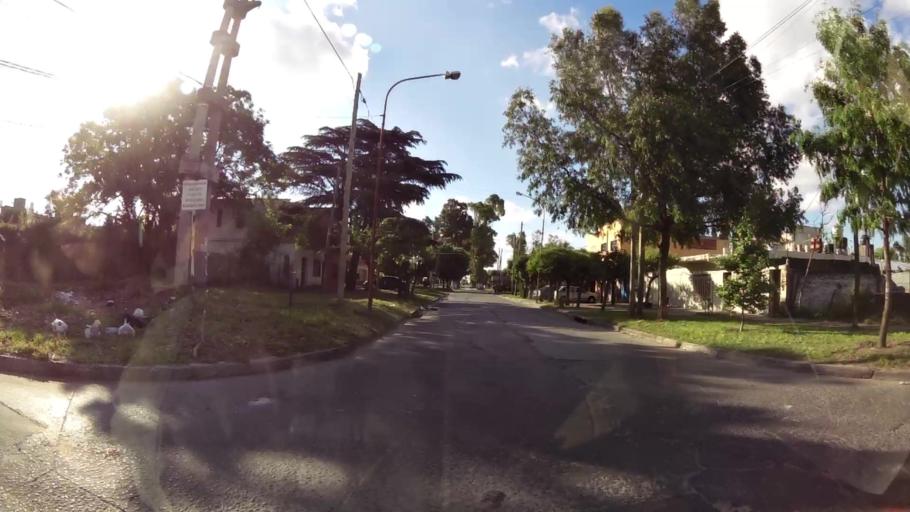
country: AR
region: Buenos Aires
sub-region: Partido de Moron
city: Moron
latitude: -34.6884
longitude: -58.6003
